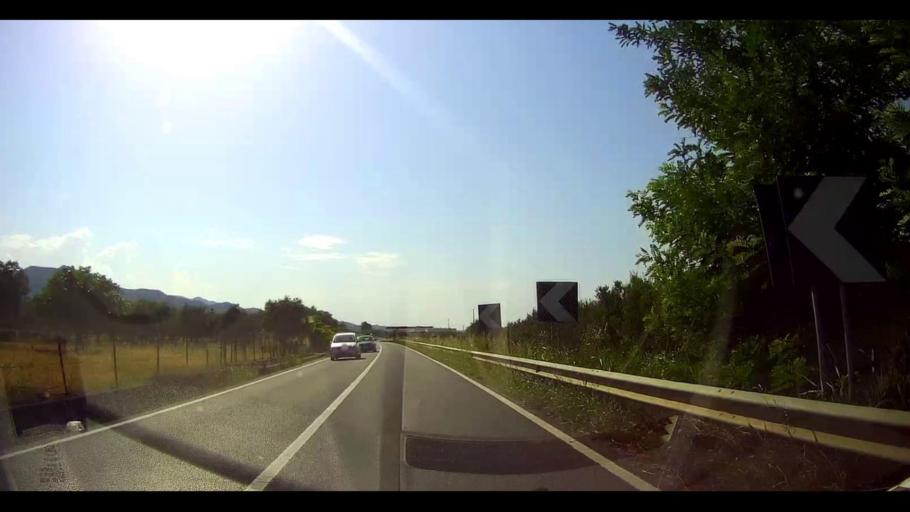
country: IT
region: Calabria
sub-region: Provincia di Cosenza
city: Cariati
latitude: 39.4784
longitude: 16.9974
